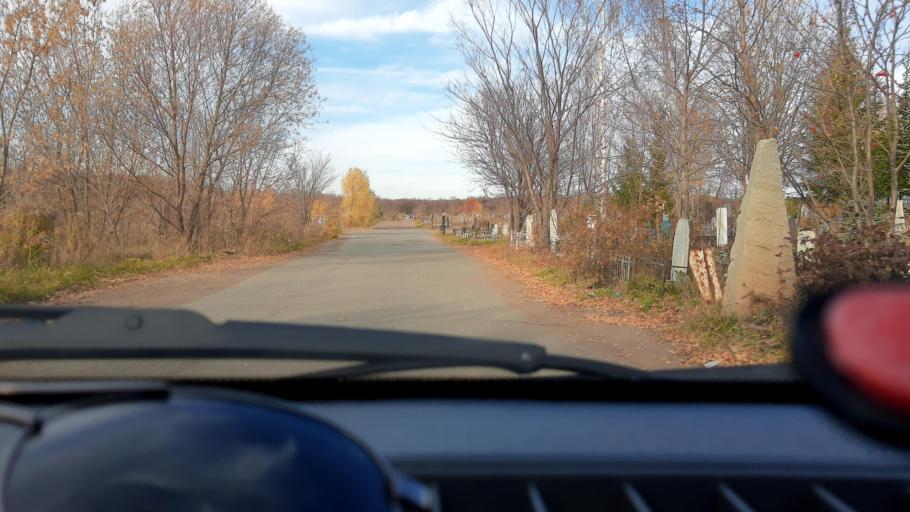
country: RU
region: Bashkortostan
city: Ufa
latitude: 54.8587
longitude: 56.1571
